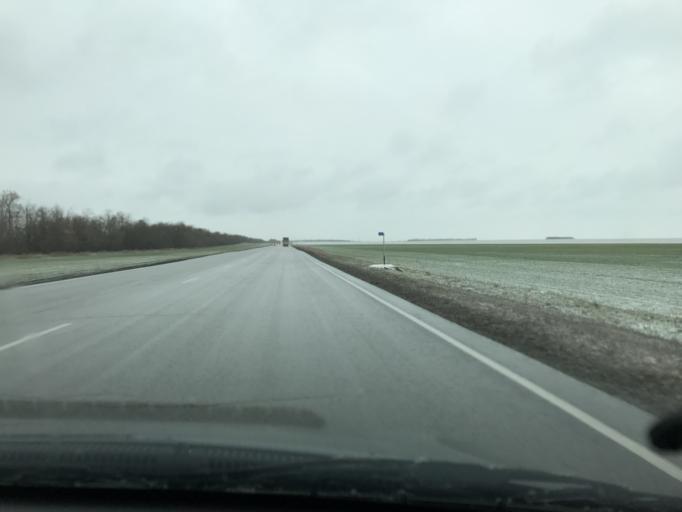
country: RU
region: Rostov
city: Kagal'nitskaya
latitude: 46.9088
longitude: 40.1155
